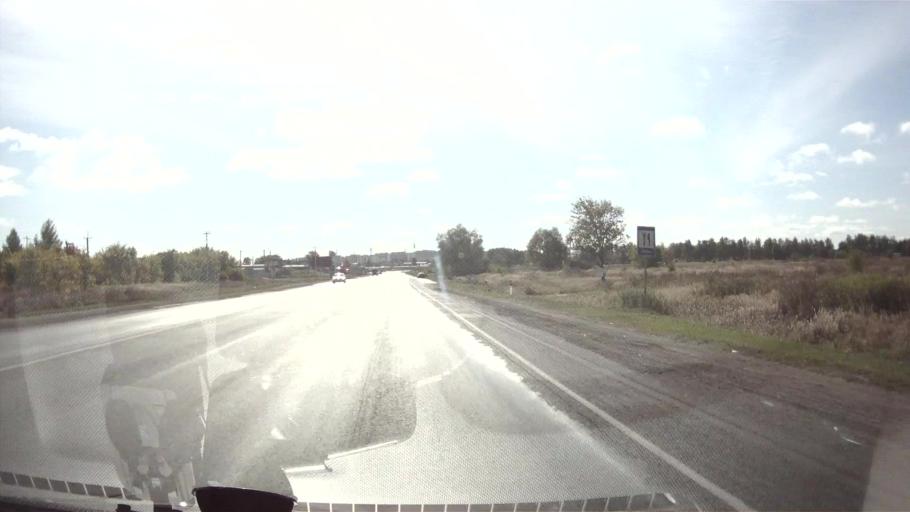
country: RU
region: Ulyanovsk
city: Isheyevka
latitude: 54.2963
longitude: 48.2491
